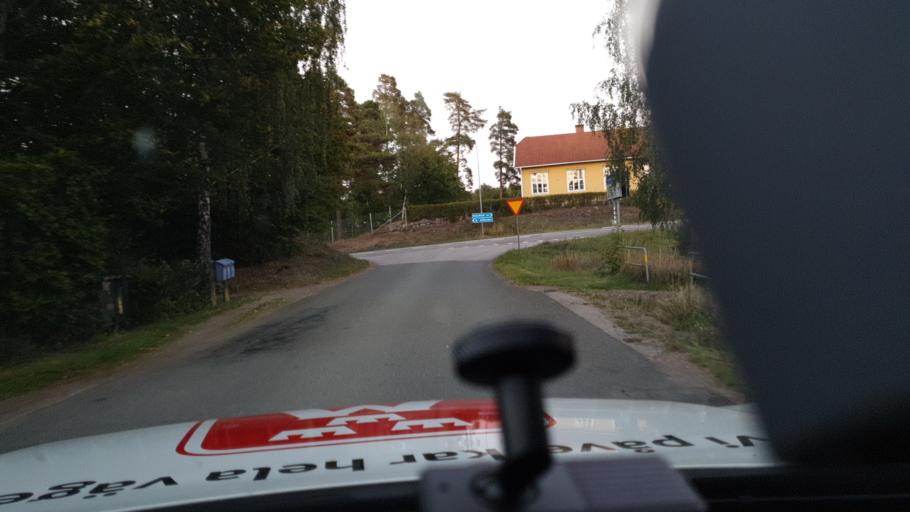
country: SE
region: Kalmar
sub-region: Hogsby Kommun
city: Hoegsby
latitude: 57.1122
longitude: 16.1041
